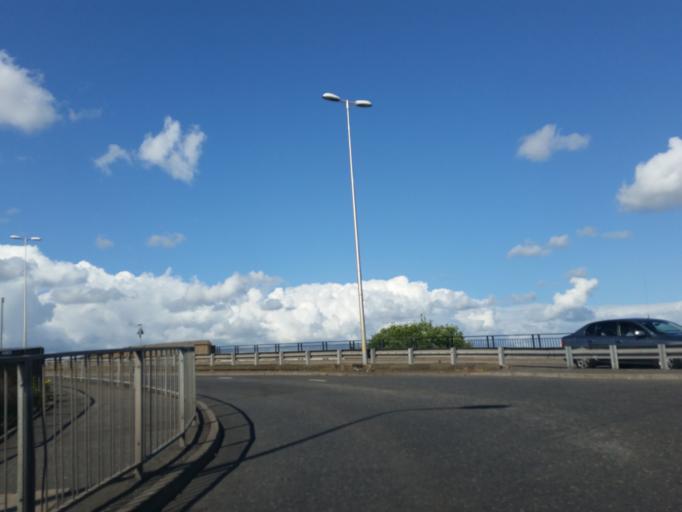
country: GB
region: Scotland
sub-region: North Lanarkshire
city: Coatbridge
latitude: 55.8540
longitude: -4.0205
